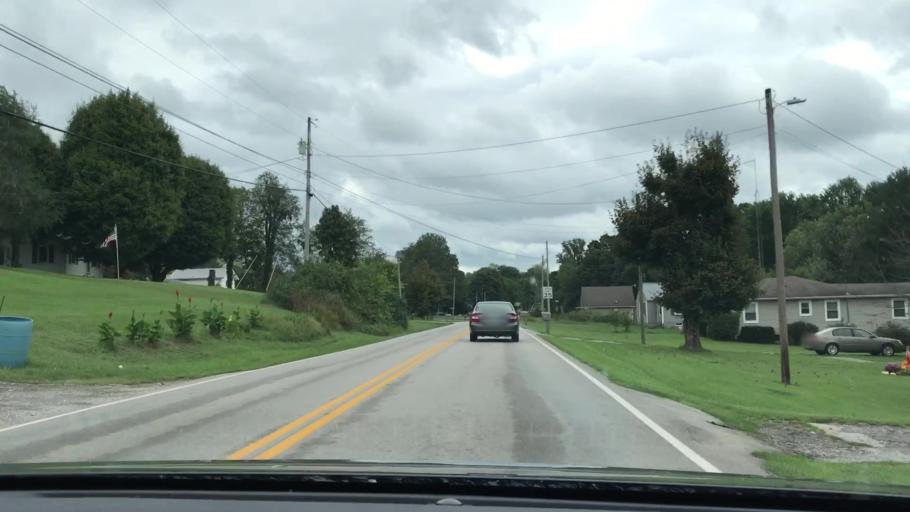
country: US
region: Kentucky
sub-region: Metcalfe County
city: Edmonton
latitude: 36.8873
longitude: -85.7118
